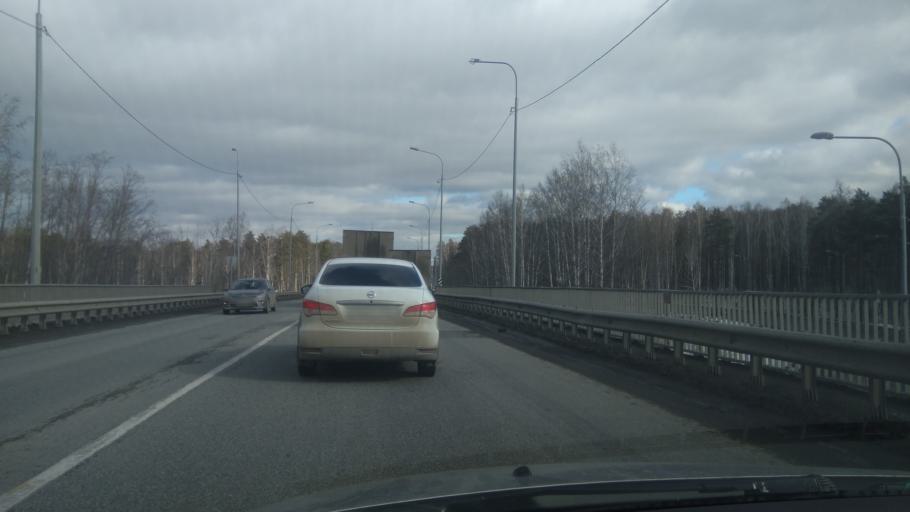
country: RU
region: Sverdlovsk
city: Talitsa
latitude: 56.8497
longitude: 60.0608
